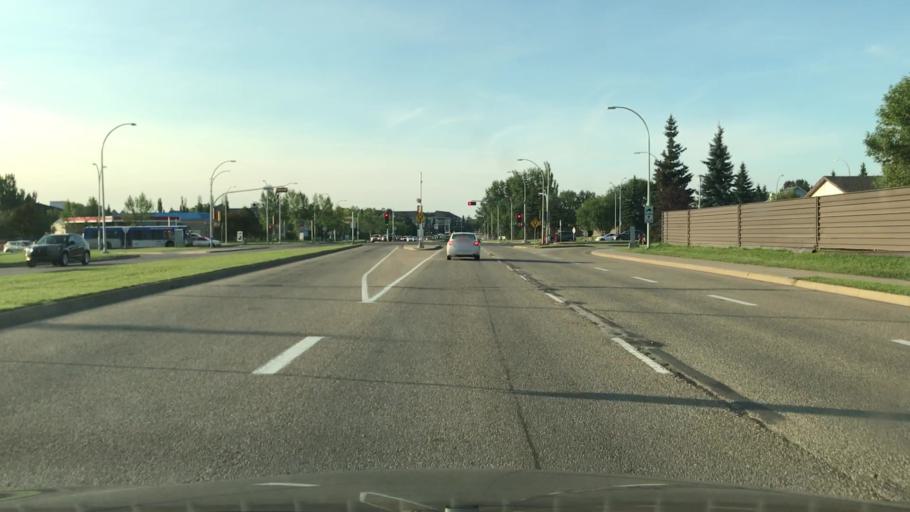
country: CA
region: Alberta
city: Beaumont
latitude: 53.4537
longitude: -113.4197
